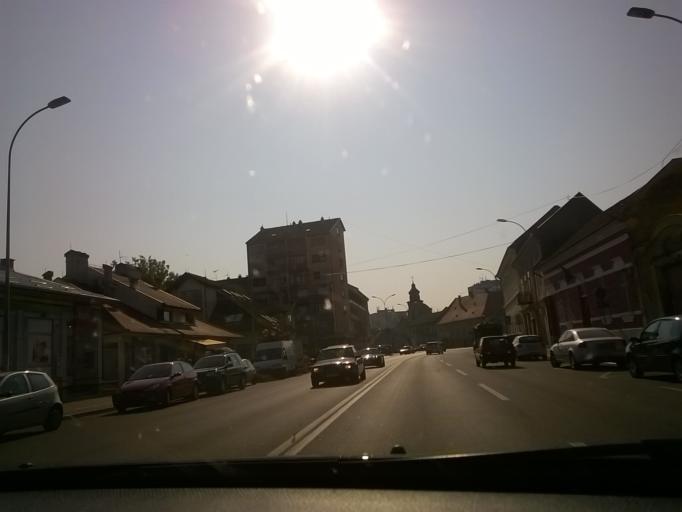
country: RS
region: Autonomna Pokrajina Vojvodina
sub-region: Juznobanatski Okrug
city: Vrsac
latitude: 45.1233
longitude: 21.2956
